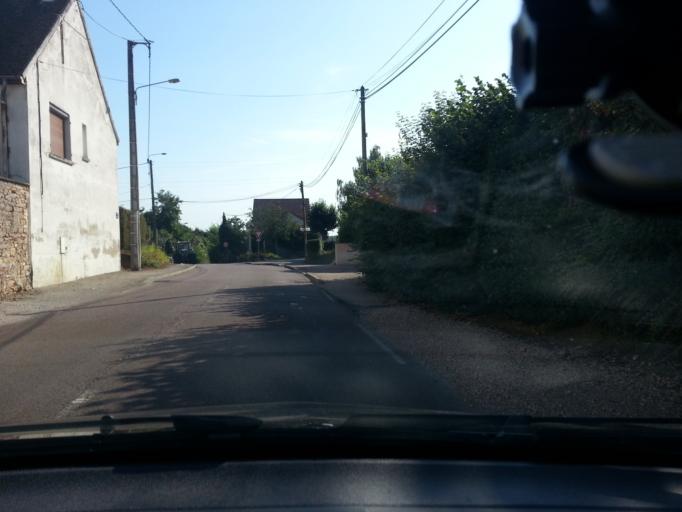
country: FR
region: Bourgogne
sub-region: Departement de Saone-et-Loire
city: Saint-Remy
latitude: 46.7652
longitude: 4.8168
